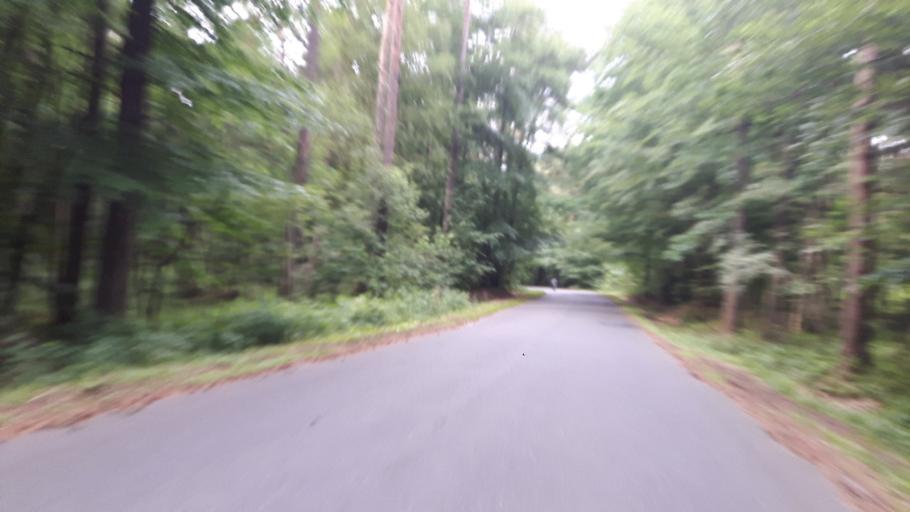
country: PL
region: West Pomeranian Voivodeship
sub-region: Powiat goleniowski
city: Nowogard
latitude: 53.7787
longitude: 15.1209
